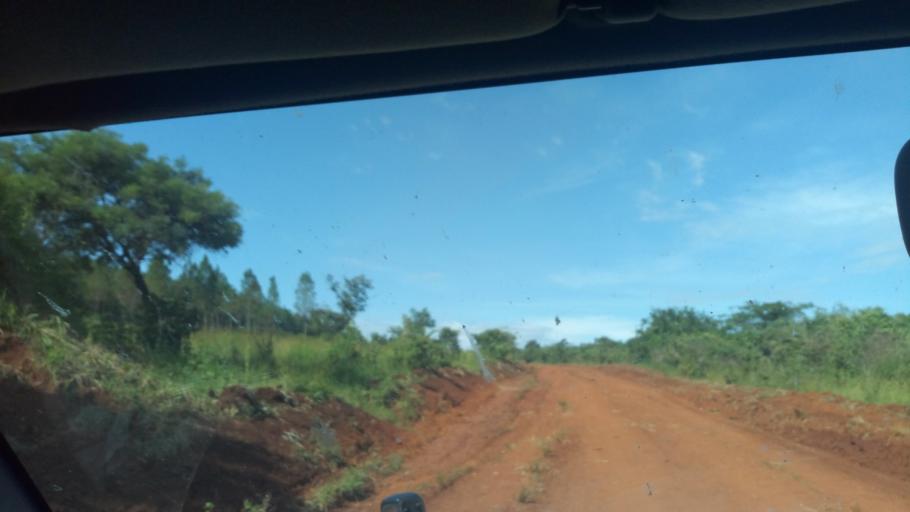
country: UG
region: Western Region
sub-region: Masindi District
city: Masindi
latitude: 1.6489
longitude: 31.7768
